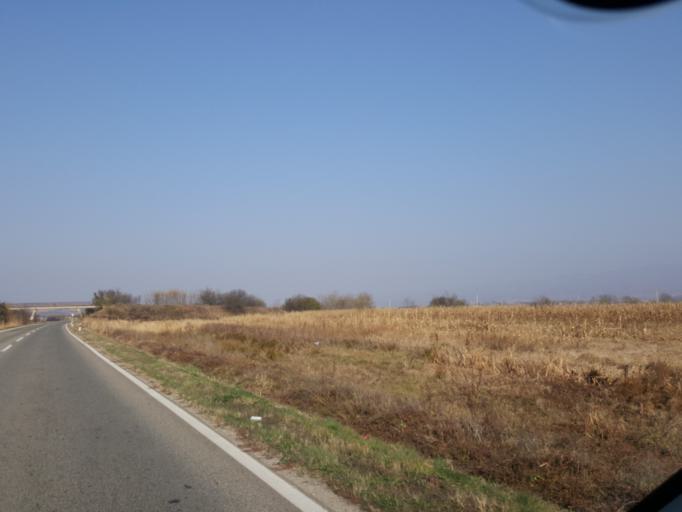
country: RS
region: Central Serbia
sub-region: Jablanicki Okrug
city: Leskovac
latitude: 43.0314
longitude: 21.9424
